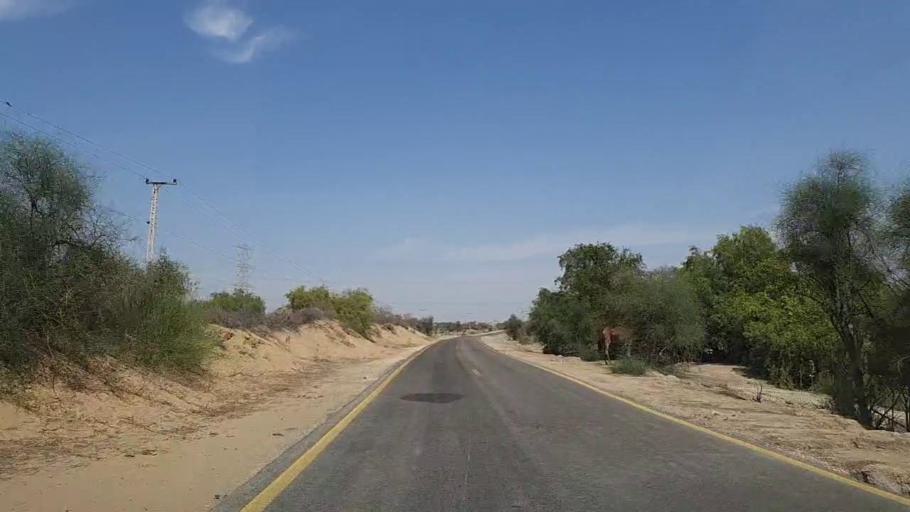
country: PK
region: Sindh
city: Mithi
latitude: 24.8491
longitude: 69.8373
